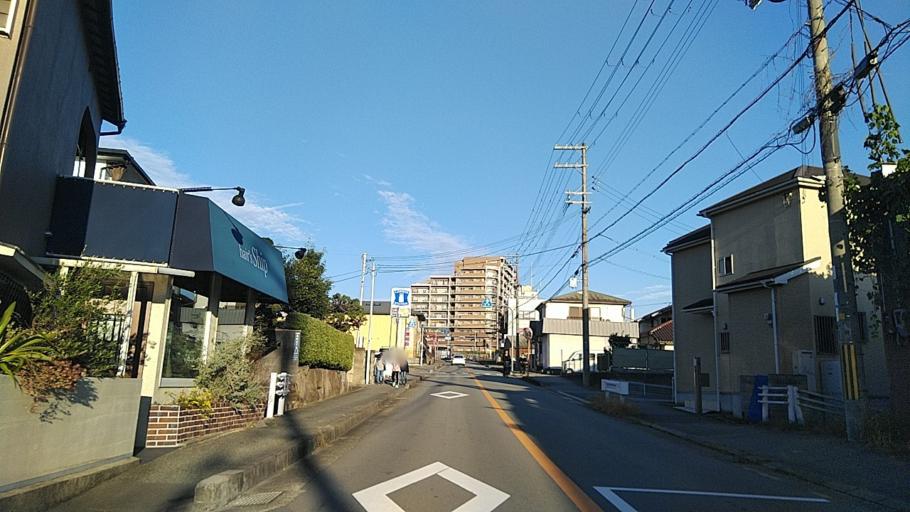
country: JP
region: Osaka
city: Ikeda
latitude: 34.8899
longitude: 135.4069
